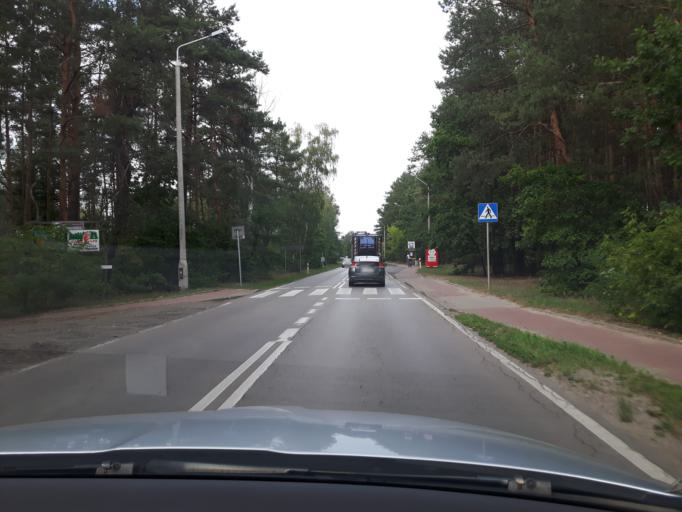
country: PL
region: Masovian Voivodeship
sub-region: Powiat legionowski
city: Stanislawow Pierwszy
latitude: 52.3851
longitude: 21.0300
